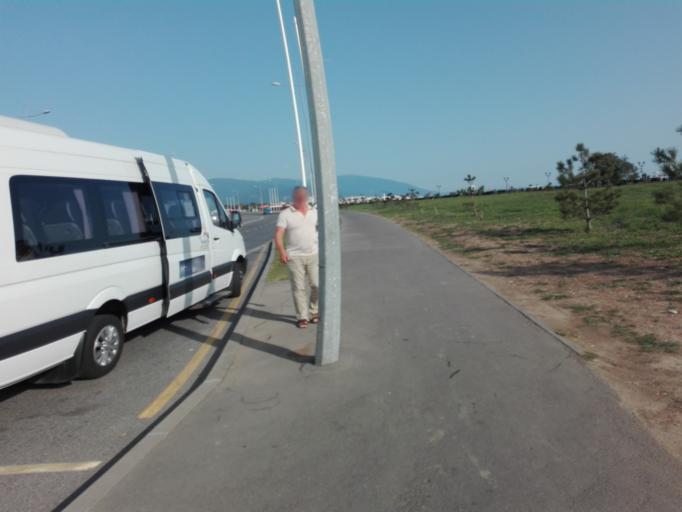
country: RU
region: Krasnodarskiy
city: Adler
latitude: 43.3996
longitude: 39.9512
